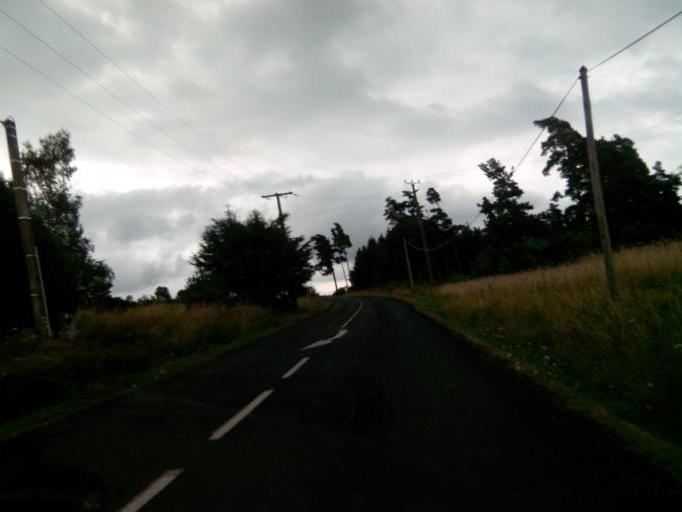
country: FR
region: Rhone-Alpes
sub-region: Departement de la Loire
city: Usson-en-Forez
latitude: 45.3548
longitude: 3.9054
